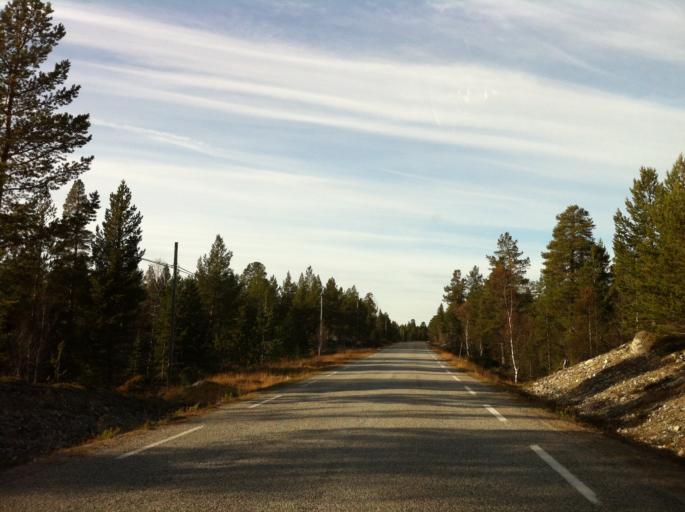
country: NO
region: Hedmark
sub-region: Engerdal
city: Engerdal
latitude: 62.1051
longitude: 12.0255
